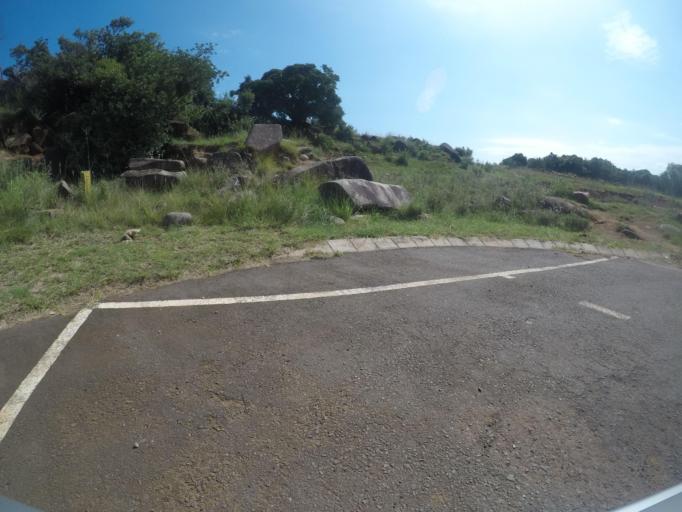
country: ZA
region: Eastern Cape
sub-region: Buffalo City Metropolitan Municipality
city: East London
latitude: -32.9640
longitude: 27.8772
